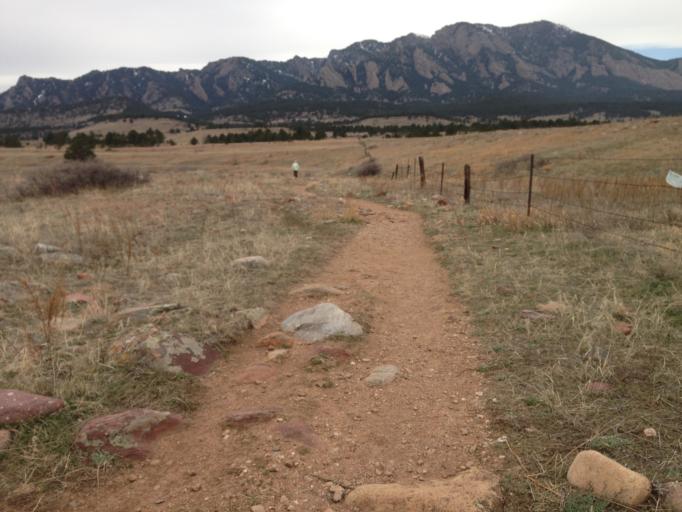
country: US
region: Colorado
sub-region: Boulder County
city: Boulder
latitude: 39.9501
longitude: -105.2485
